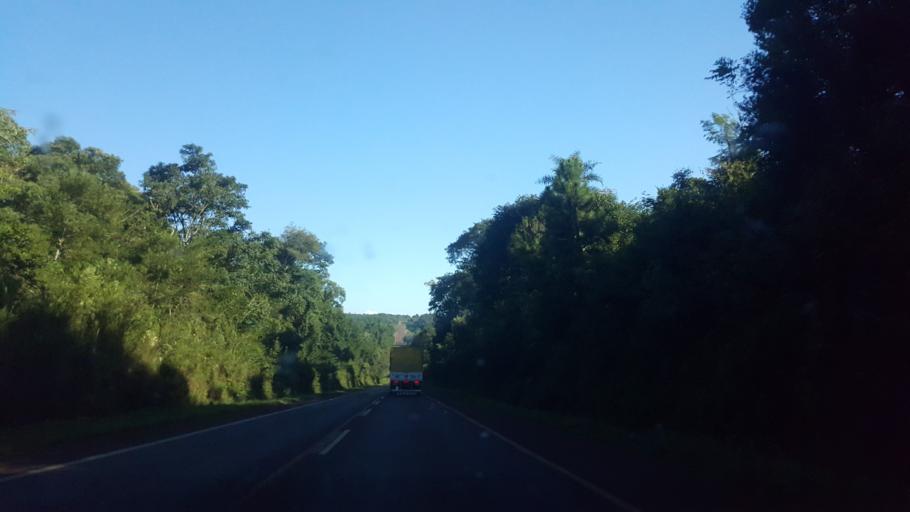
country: AR
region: Misiones
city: Puerto Esperanza
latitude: -26.1907
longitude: -54.5886
